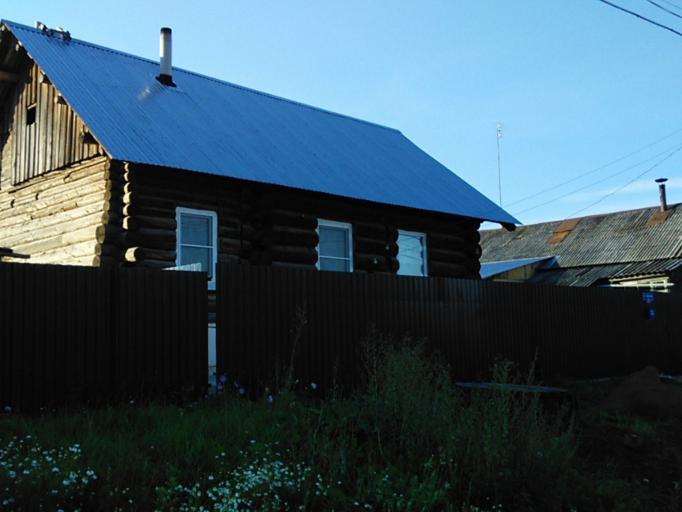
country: RU
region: Perm
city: Foki
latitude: 56.6892
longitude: 54.3450
